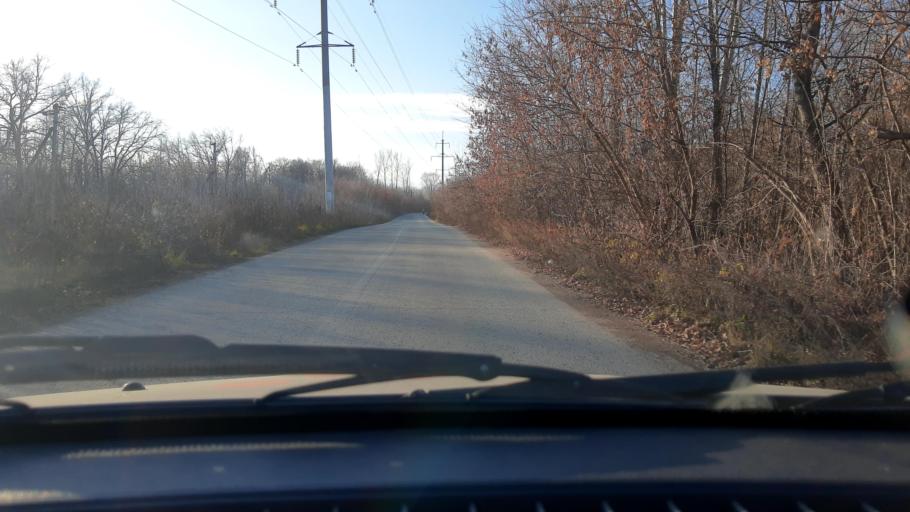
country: RU
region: Bashkortostan
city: Ufa
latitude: 54.6649
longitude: 55.9547
